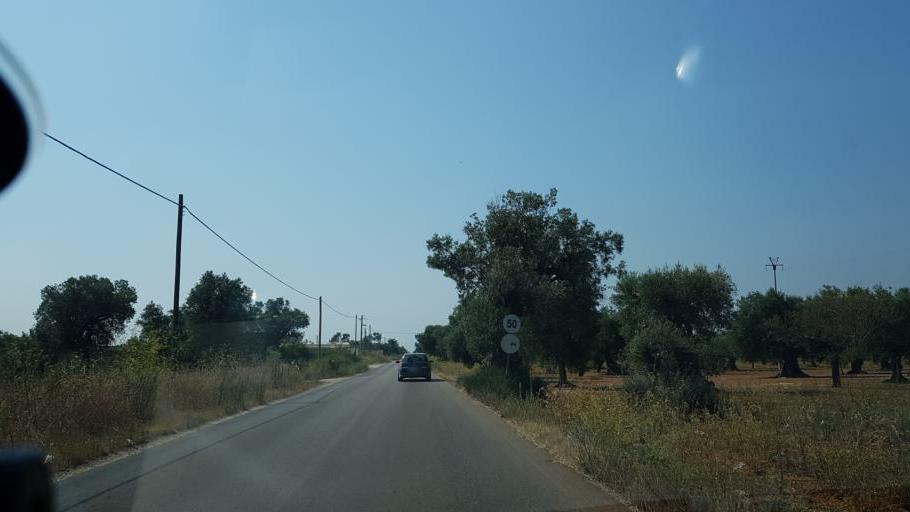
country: IT
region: Apulia
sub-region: Provincia di Taranto
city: Manduria
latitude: 40.4168
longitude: 17.6321
